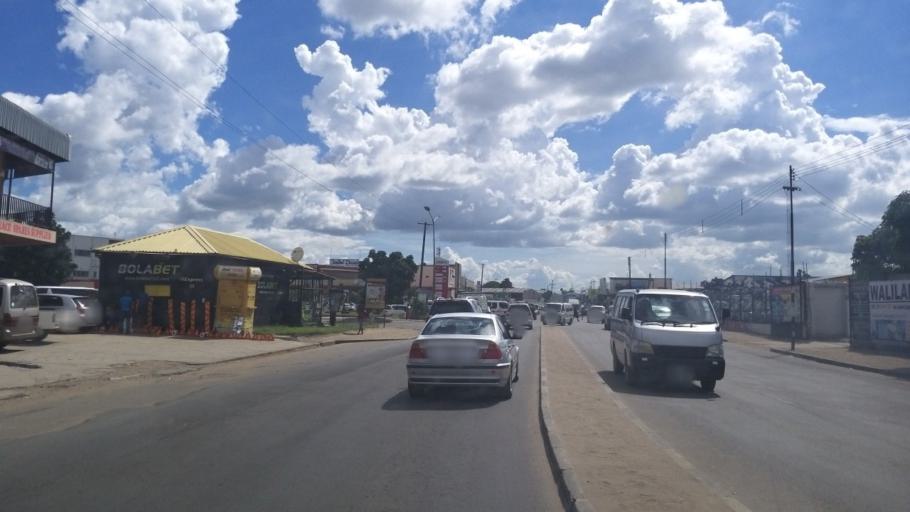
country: ZM
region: Lusaka
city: Lusaka
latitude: -15.4107
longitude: 28.2781
